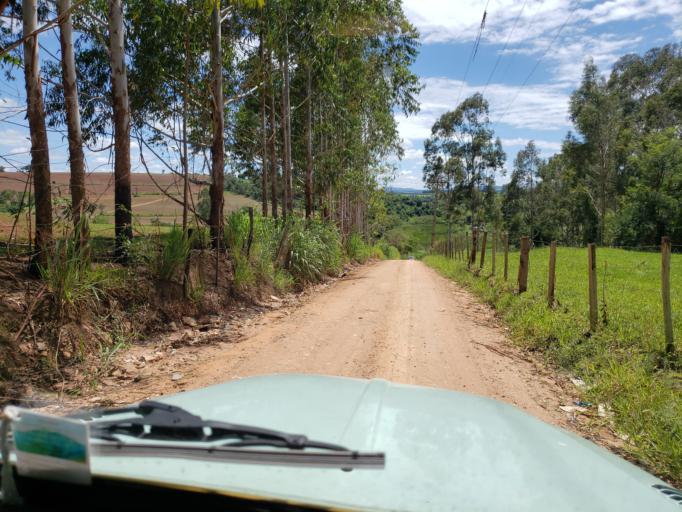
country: BR
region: Sao Paulo
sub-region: Moji-Guacu
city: Mogi-Gaucu
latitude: -22.3021
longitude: -46.9037
